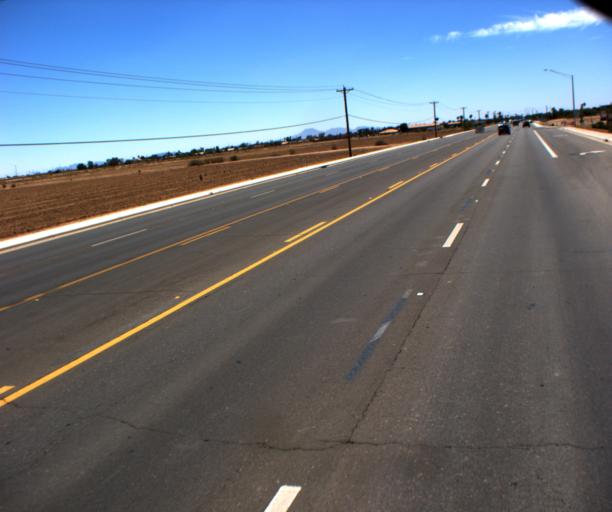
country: US
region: Arizona
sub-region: Pinal County
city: Casa Grande
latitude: 32.8797
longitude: -111.6996
